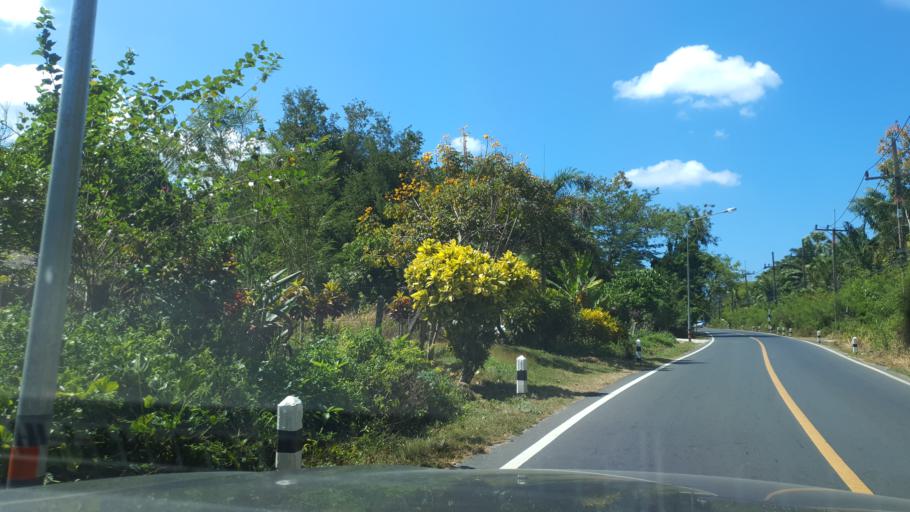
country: TH
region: Phuket
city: Thalang
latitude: 8.1243
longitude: 98.3194
